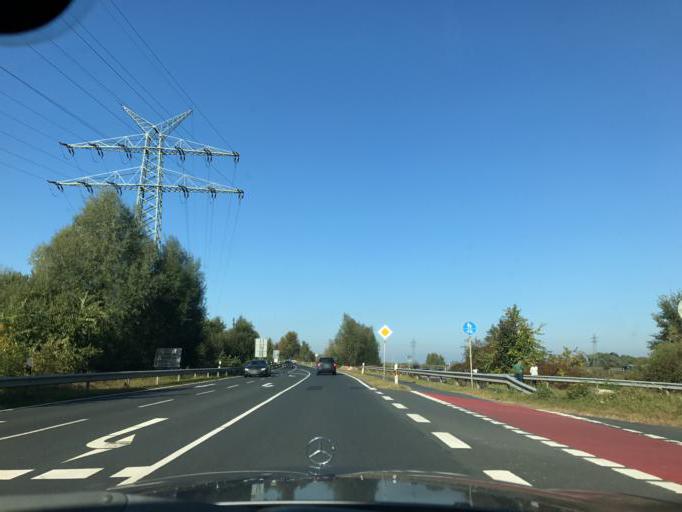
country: DE
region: Lower Saxony
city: Papenburg
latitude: 53.0983
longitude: 7.3544
